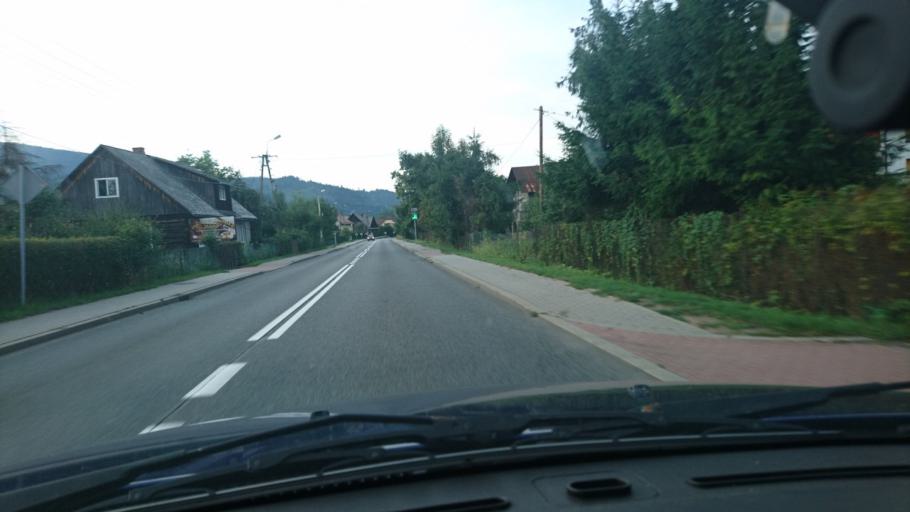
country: PL
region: Silesian Voivodeship
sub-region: Powiat zywiecki
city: Cisiec
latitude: 49.5968
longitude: 19.1074
